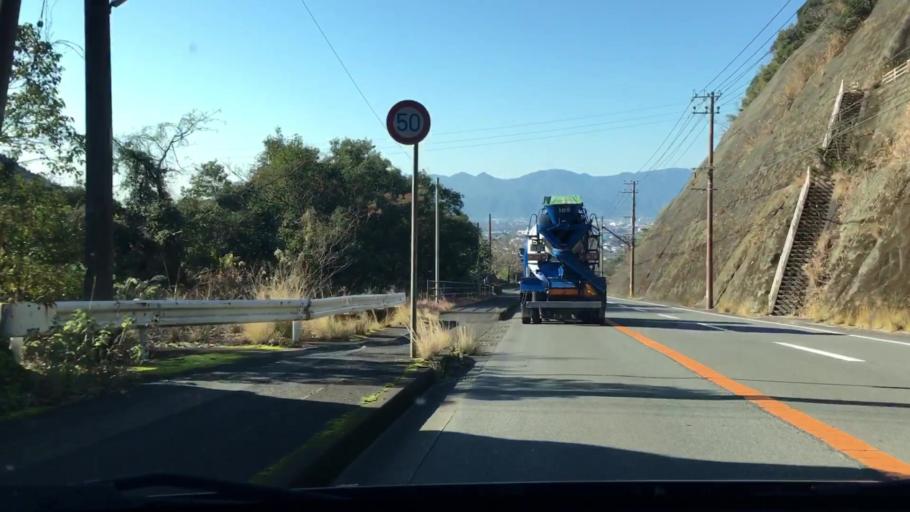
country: JP
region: Kagoshima
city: Kajiki
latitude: 31.7524
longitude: 130.6771
